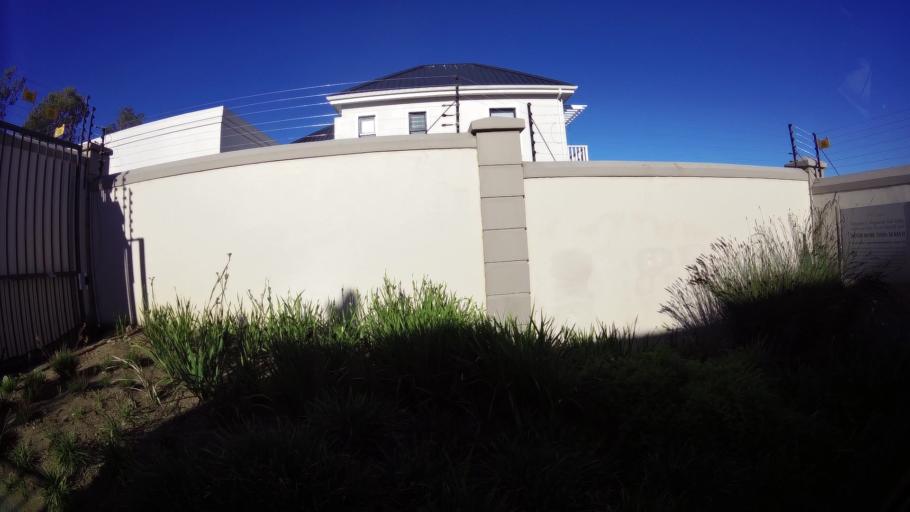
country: ZA
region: Western Cape
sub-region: Eden District Municipality
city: George
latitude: -33.9646
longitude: 22.4385
